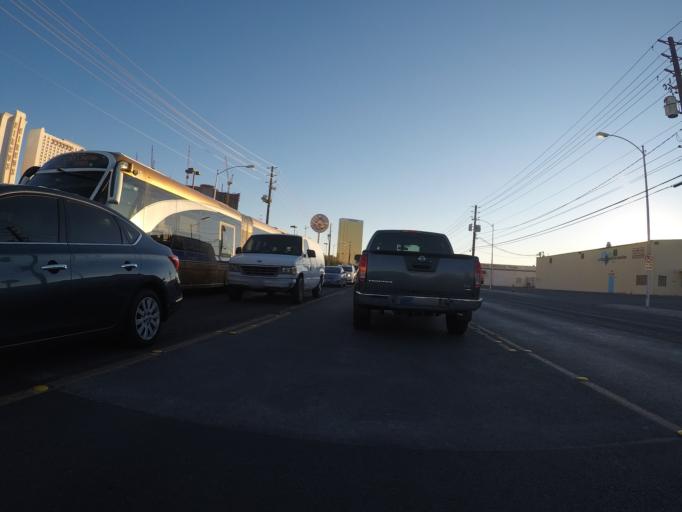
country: US
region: Nevada
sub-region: Clark County
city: Las Vegas
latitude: 36.1411
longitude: -115.1667
